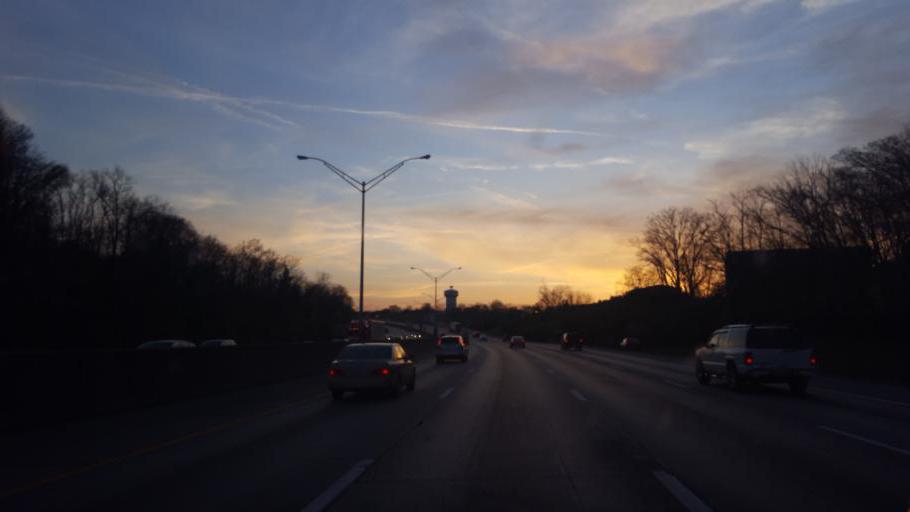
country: US
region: Kentucky
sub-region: Kenton County
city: Fort Wright
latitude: 39.0609
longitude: -84.5300
